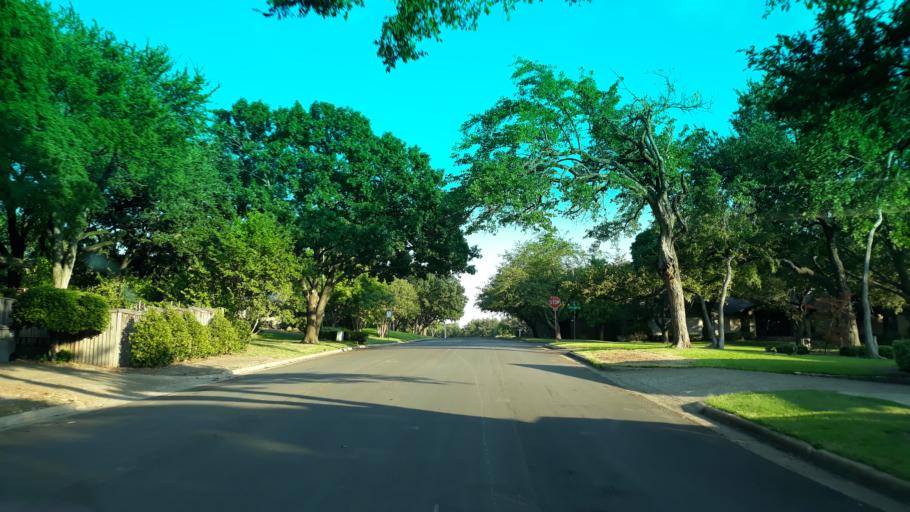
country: US
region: Texas
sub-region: Dallas County
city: Addison
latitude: 32.9445
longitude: -96.7907
